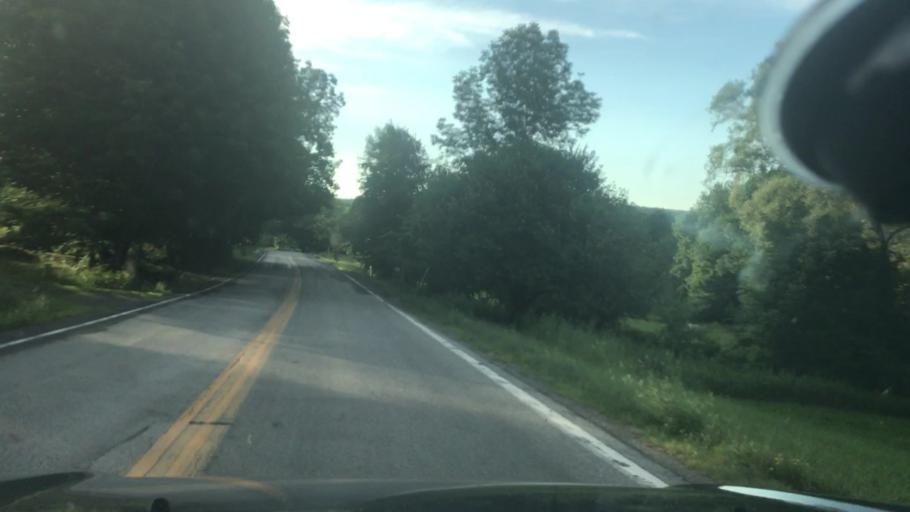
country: US
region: New York
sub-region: Otsego County
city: Unadilla
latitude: 42.3328
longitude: -75.2356
